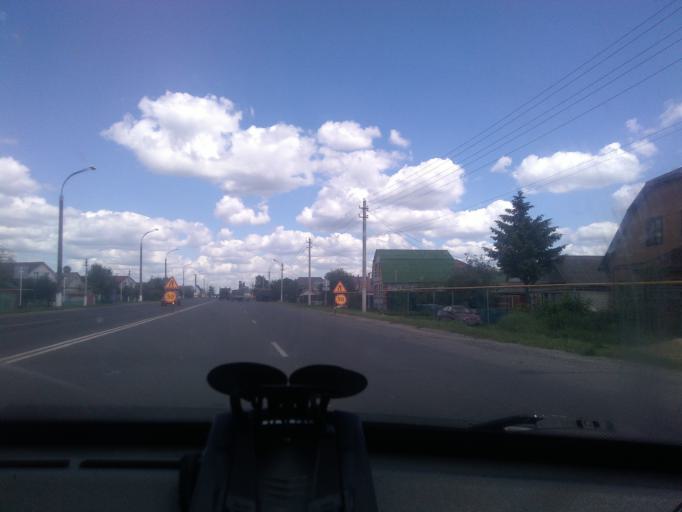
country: RU
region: Kursk
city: Voroshnevo
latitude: 51.6507
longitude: 35.9888
